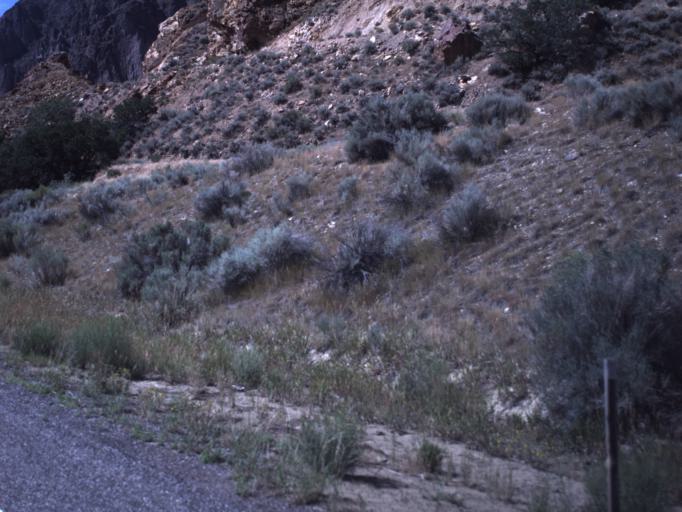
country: US
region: Utah
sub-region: Sevier County
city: Monroe
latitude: 38.5088
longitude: -112.2598
